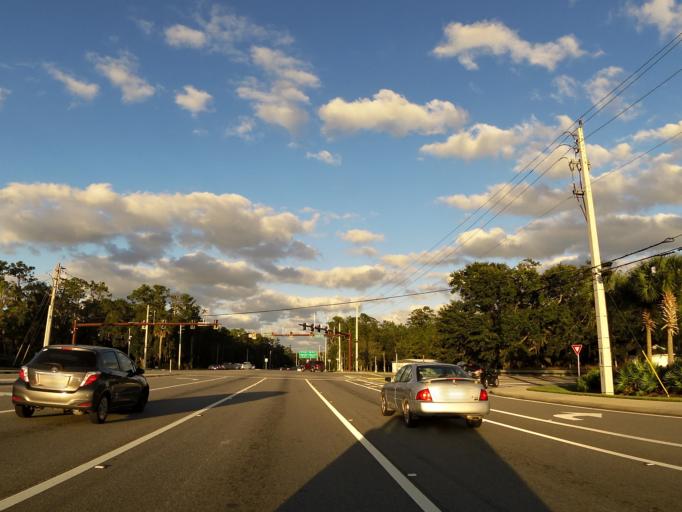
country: US
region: Florida
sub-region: Saint Johns County
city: Fruit Cove
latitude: 30.0628
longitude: -81.5050
